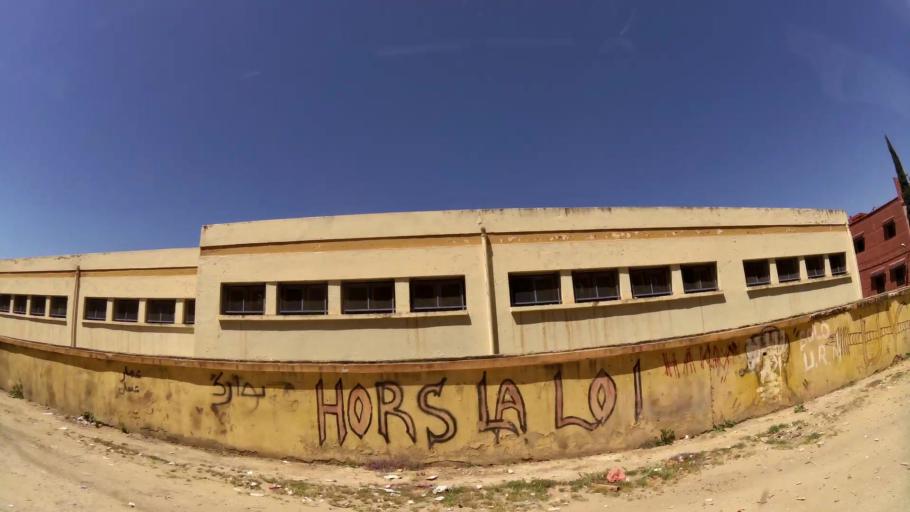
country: MA
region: Meknes-Tafilalet
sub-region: Meknes
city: Meknes
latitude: 33.8770
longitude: -5.5653
